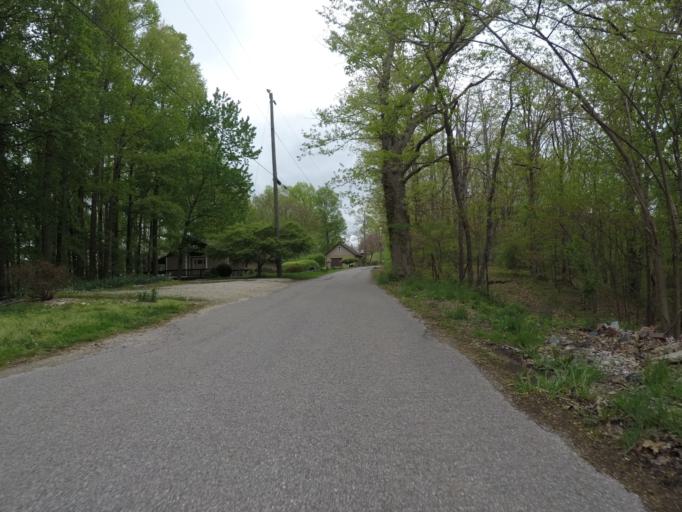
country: US
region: West Virginia
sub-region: Cabell County
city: Barboursville
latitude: 38.3994
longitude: -82.2610
